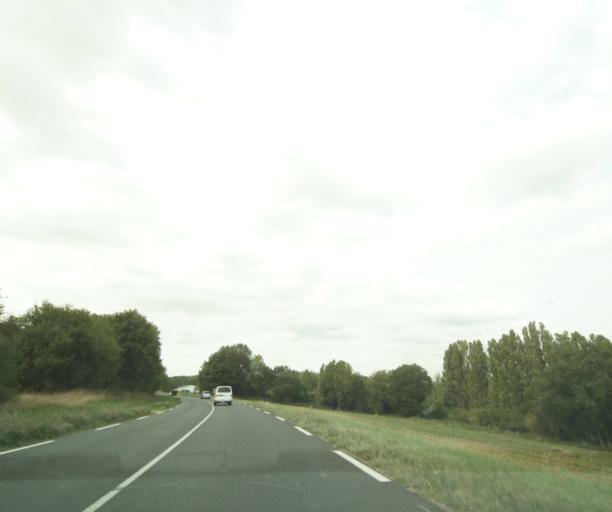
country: FR
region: Centre
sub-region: Departement de l'Indre
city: Chatillon-sur-Indre
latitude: 47.0451
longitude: 1.0952
